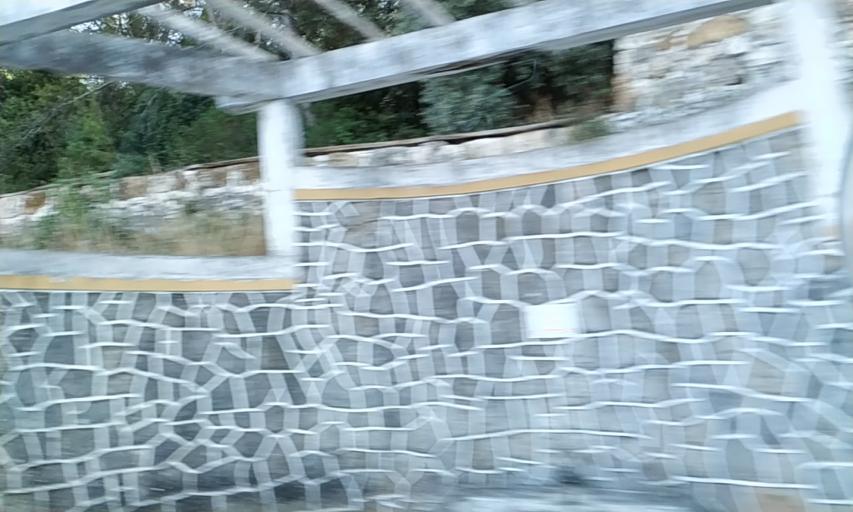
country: PT
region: Santarem
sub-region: Alcanena
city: Alcanena
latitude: 39.3870
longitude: -8.6543
